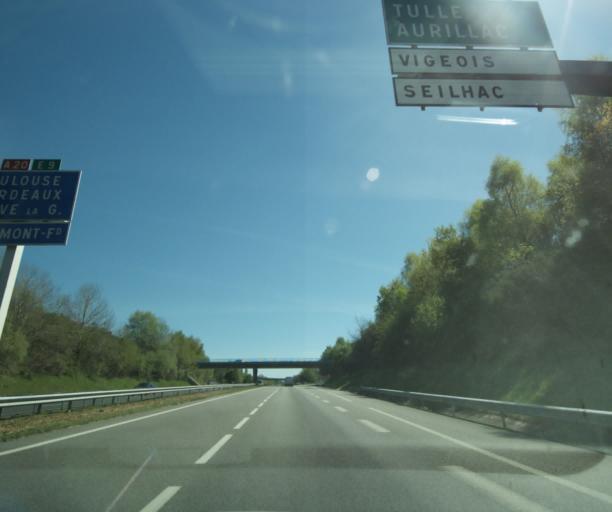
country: FR
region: Limousin
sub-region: Departement de la Correze
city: Uzerche
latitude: 45.3969
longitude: 1.5668
